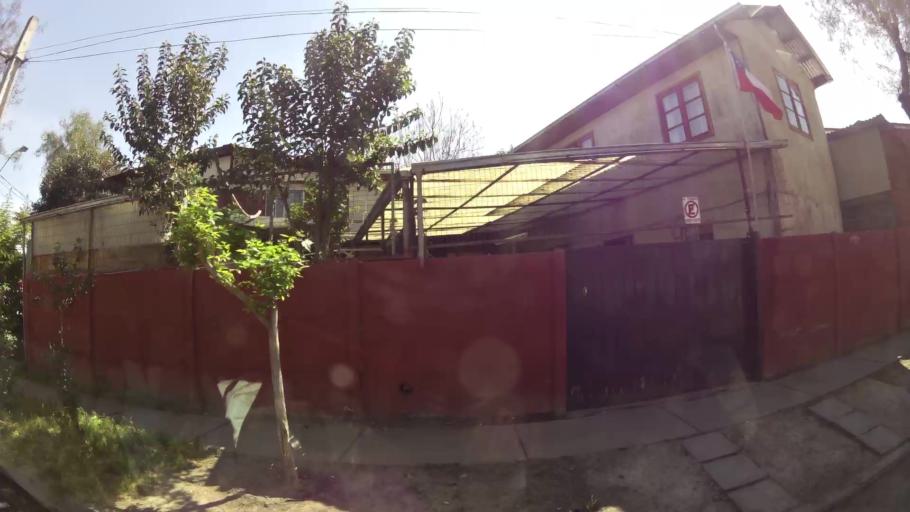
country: CL
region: Santiago Metropolitan
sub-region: Provincia de Santiago
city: Villa Presidente Frei, Nunoa, Santiago, Chile
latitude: -33.5301
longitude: -70.5635
